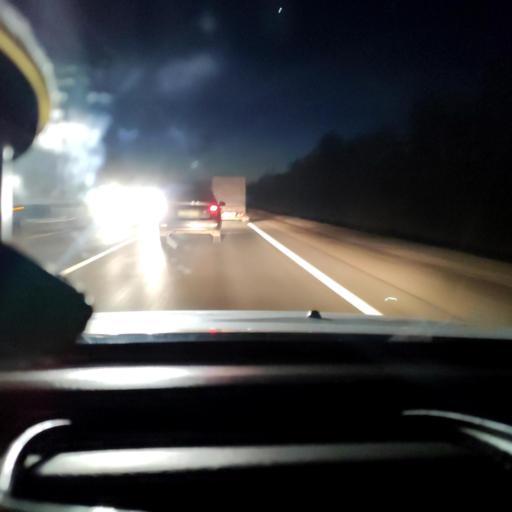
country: RU
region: Samara
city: Novokuybyshevsk
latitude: 52.9891
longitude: 49.8513
